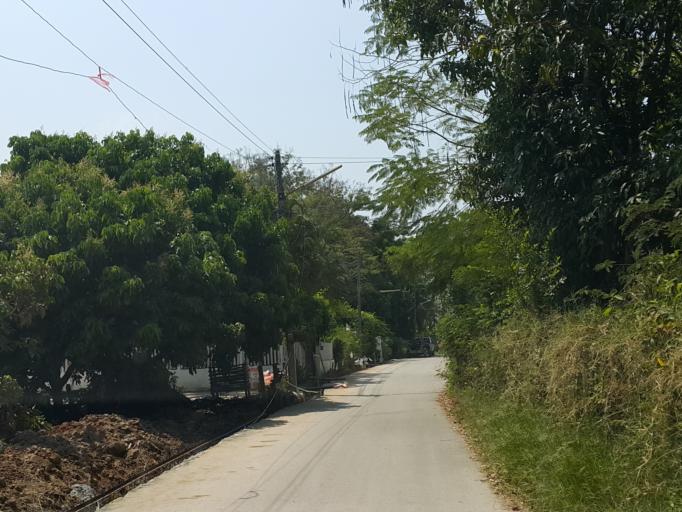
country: TH
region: Chiang Mai
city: Saraphi
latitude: 18.7358
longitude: 98.9930
